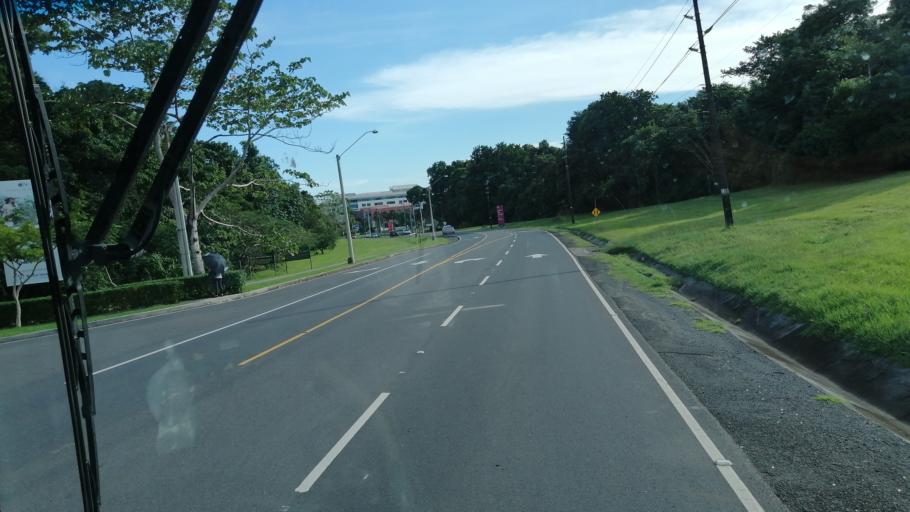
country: PA
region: Panama
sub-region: Distrito de Panama
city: Ancon
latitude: 8.9317
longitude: -79.5915
